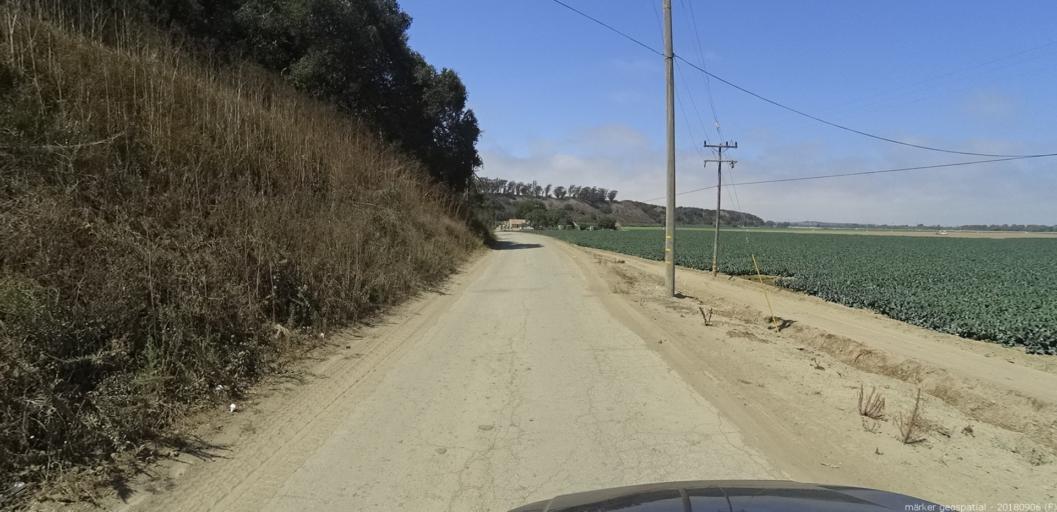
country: US
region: California
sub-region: Monterey County
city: Boronda
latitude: 36.6572
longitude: -121.7333
